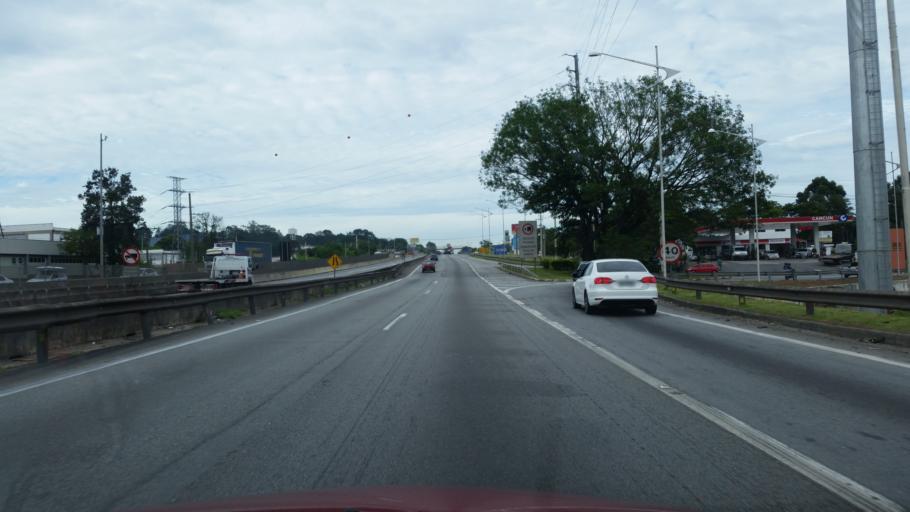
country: BR
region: Sao Paulo
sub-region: Embu
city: Embu
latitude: -23.6409
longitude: -46.8369
